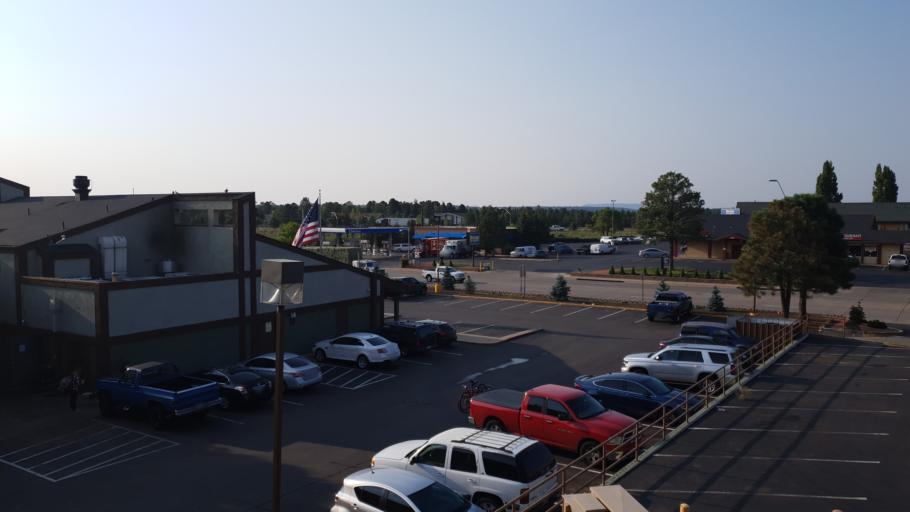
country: US
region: Arizona
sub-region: Coconino County
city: Flagstaff
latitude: 35.1928
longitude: -111.6248
